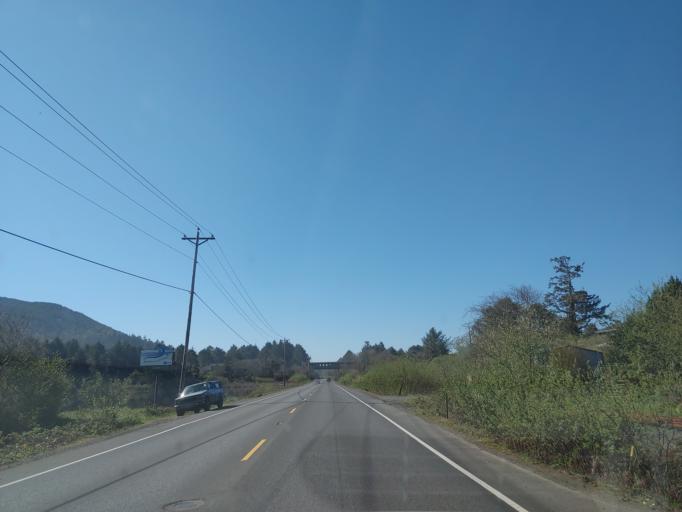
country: US
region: Oregon
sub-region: Tillamook County
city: Rockaway Beach
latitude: 45.5978
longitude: -123.9465
